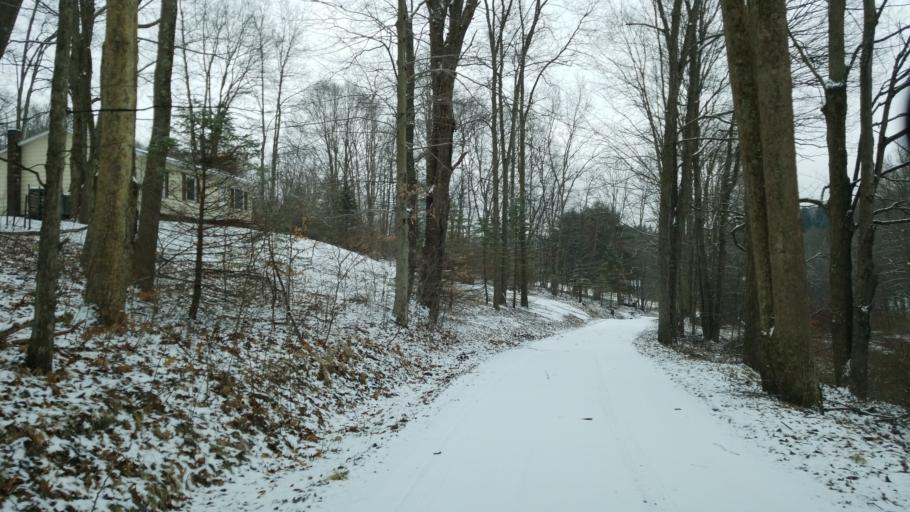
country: US
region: Pennsylvania
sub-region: Jefferson County
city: Sykesville
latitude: 41.0636
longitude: -78.8244
